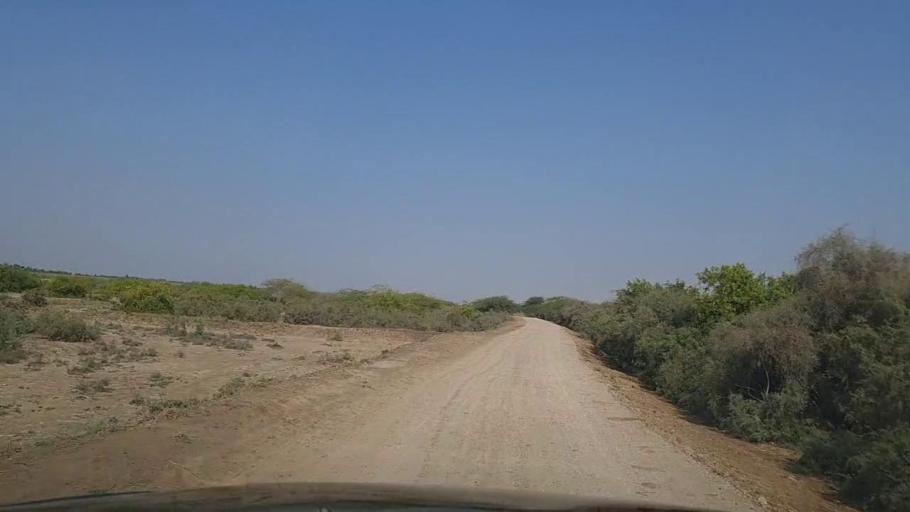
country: PK
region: Sindh
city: Thatta
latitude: 24.6477
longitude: 67.8170
